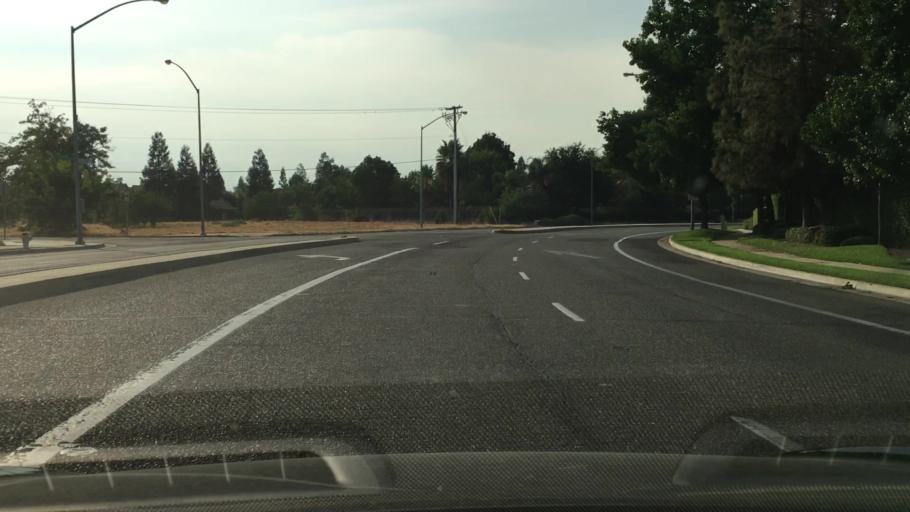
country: US
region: California
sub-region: Fresno County
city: Clovis
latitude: 36.8406
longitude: -119.7380
